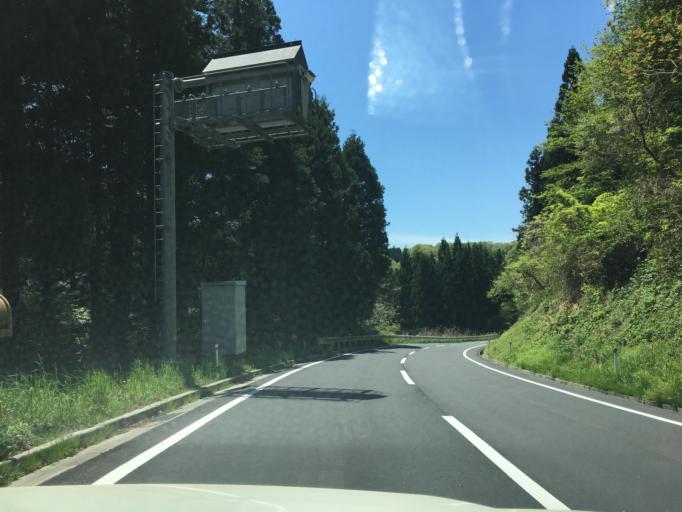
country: JP
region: Fukushima
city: Funehikimachi-funehiki
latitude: 37.3372
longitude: 140.6295
